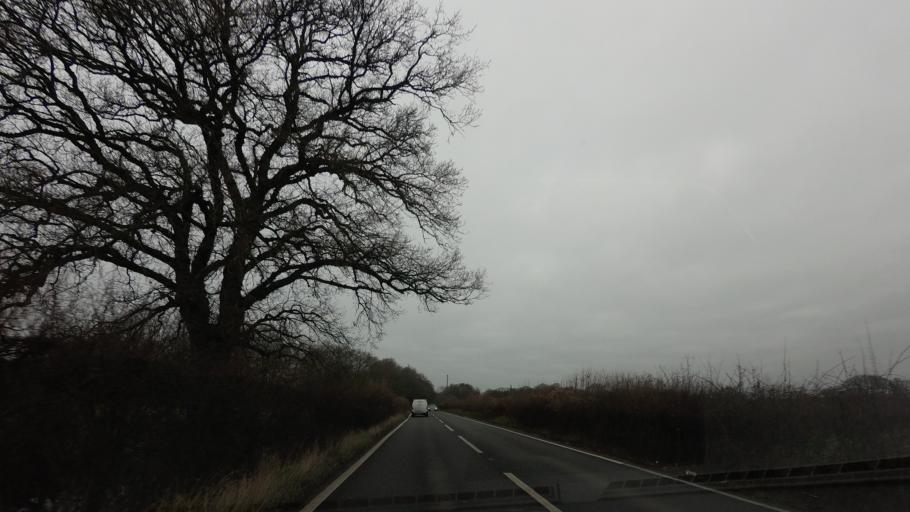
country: GB
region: England
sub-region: East Sussex
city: Saint Leonards-on-Sea
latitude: 50.9048
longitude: 0.5501
